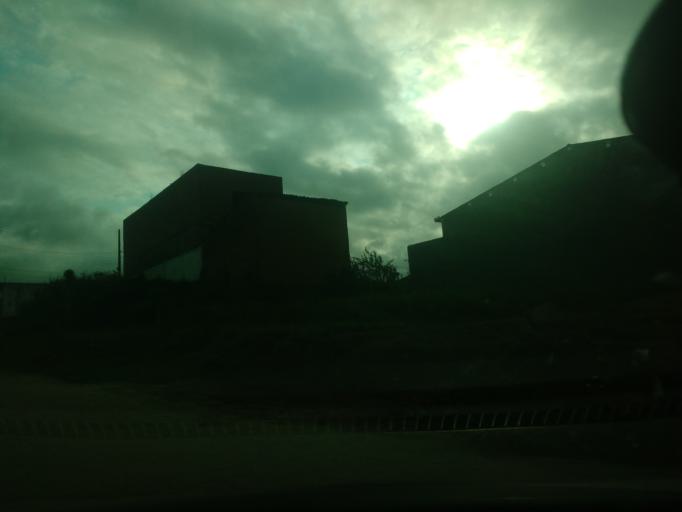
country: BR
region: Alagoas
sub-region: Uniao Dos Palmares
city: Uniao dos Palmares
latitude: -9.1517
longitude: -36.0216
